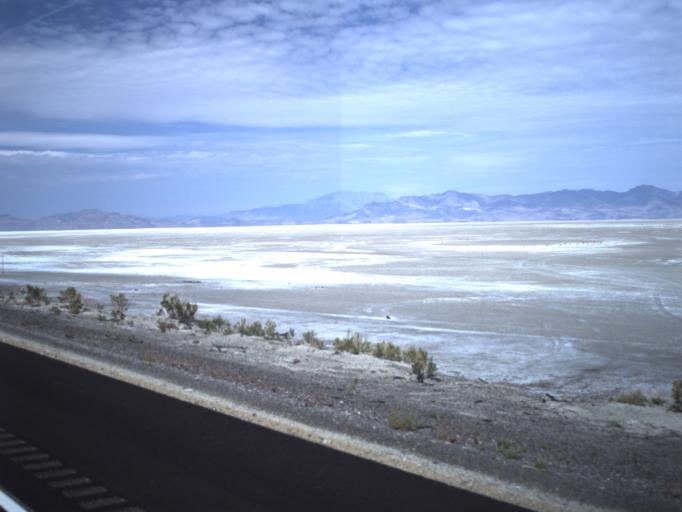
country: US
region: Utah
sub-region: Tooele County
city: Wendover
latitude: 40.7342
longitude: -113.6036
